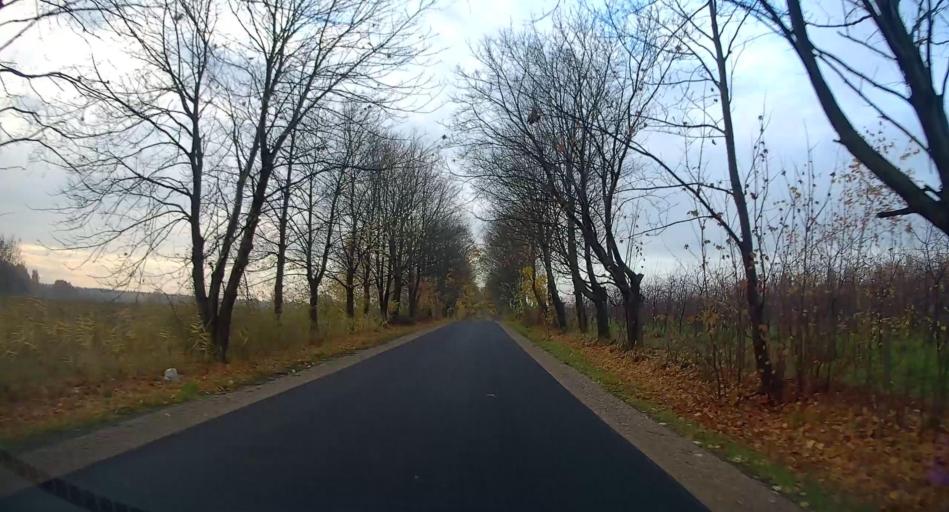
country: PL
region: Masovian Voivodeship
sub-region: Powiat zyrardowski
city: Puszcza Marianska
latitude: 51.9480
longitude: 20.3717
